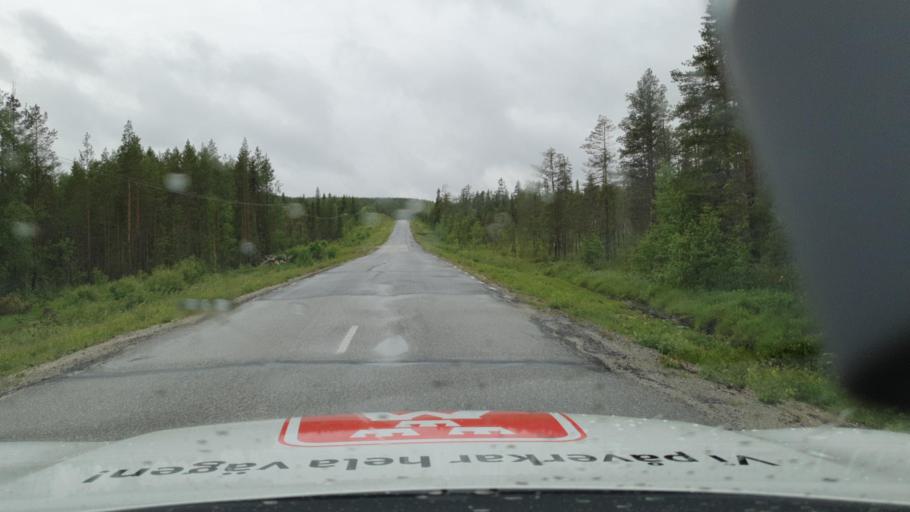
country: SE
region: Vaesterbotten
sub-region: Asele Kommun
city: Asele
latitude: 64.0074
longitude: 17.2348
